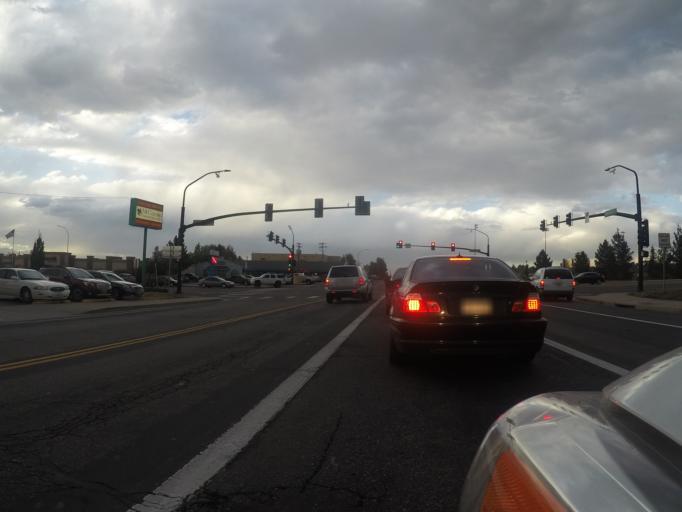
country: US
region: Colorado
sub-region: Arapahoe County
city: Littleton
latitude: 39.6237
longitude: -105.0067
